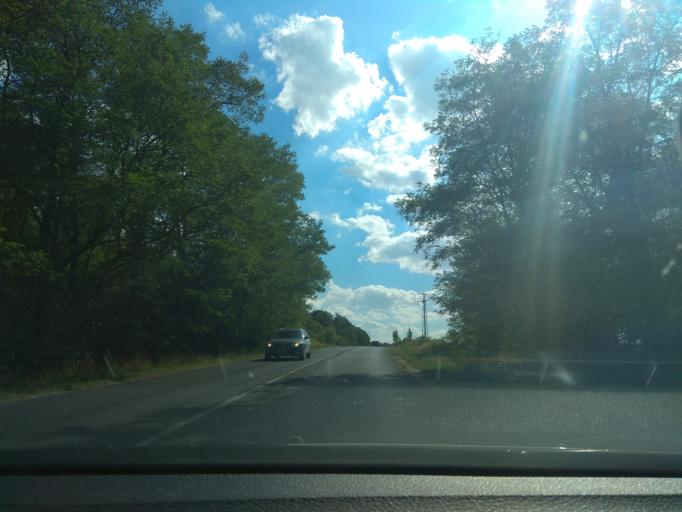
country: HU
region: Borsod-Abauj-Zemplen
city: Malyi
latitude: 48.0466
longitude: 20.7926
